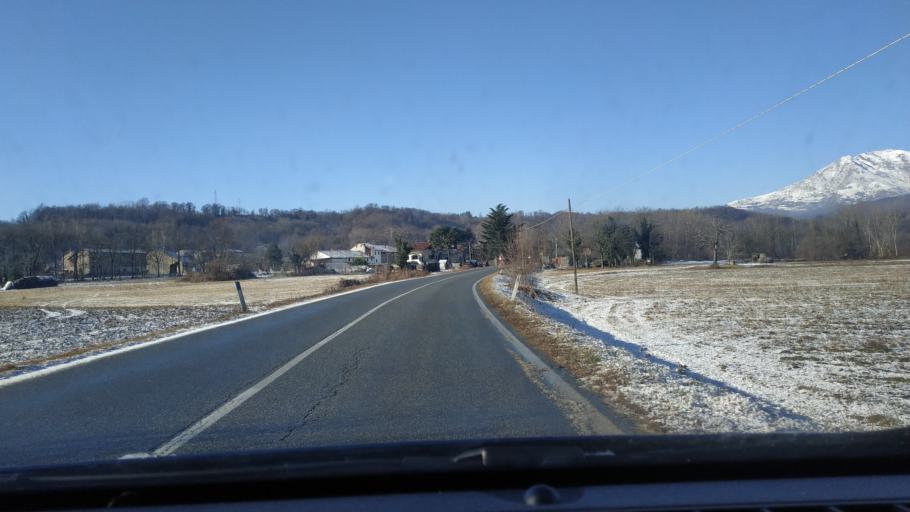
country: IT
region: Piedmont
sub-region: Provincia di Torino
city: San Martino Canavese
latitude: 45.4094
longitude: 7.8147
